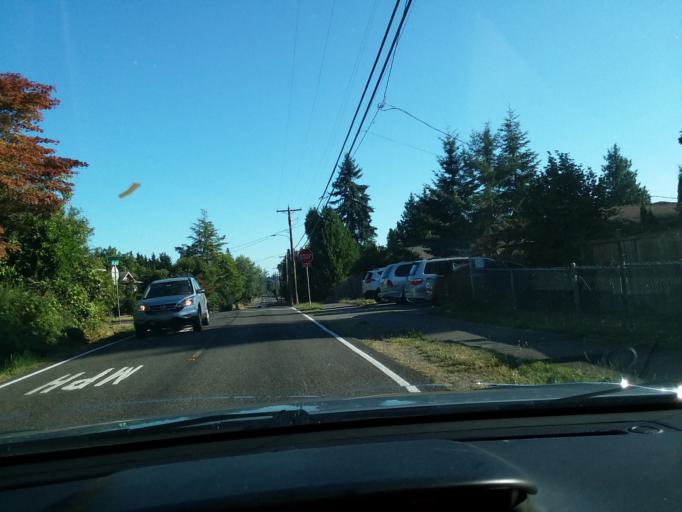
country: US
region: Washington
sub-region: Snohomish County
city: Alderwood Manor
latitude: 47.8264
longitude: -122.2871
